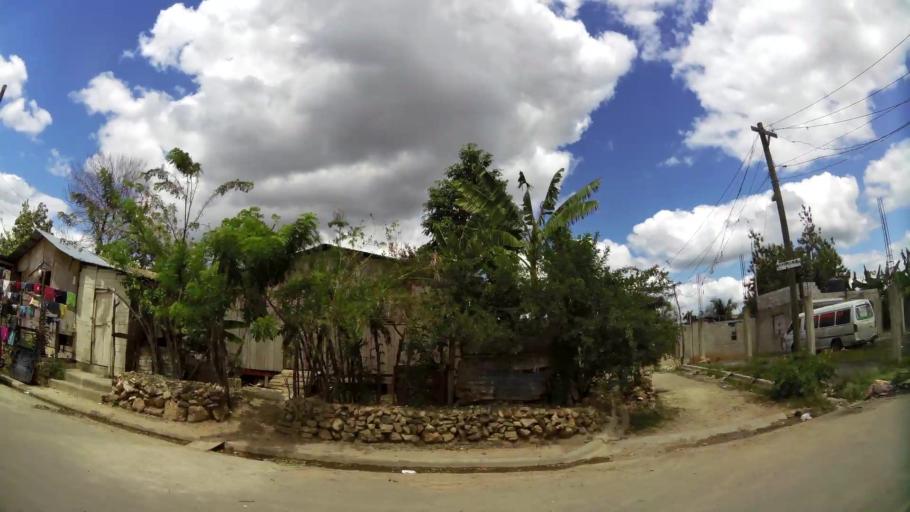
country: DO
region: Nacional
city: Ensanche Luperon
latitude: 18.5128
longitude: -69.9033
